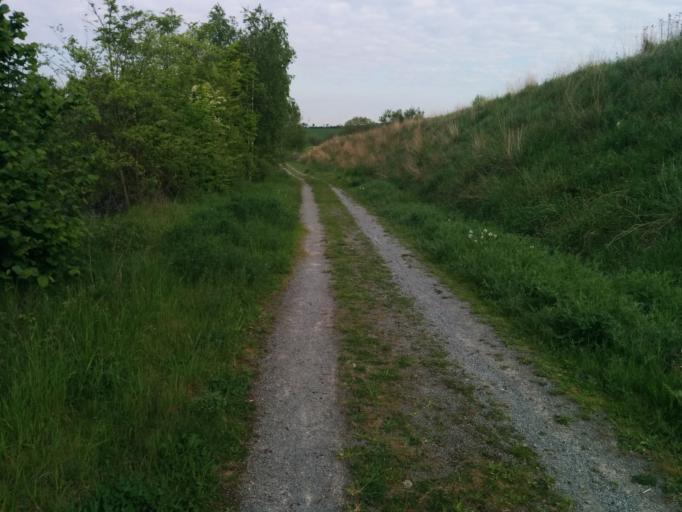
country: DE
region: Lower Saxony
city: Wolfsburg
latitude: 52.4511
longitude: 10.7808
